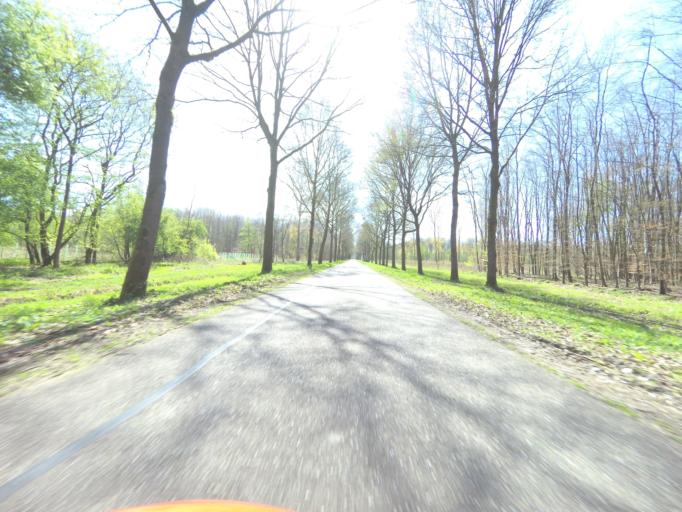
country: NL
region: Flevoland
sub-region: Gemeente Zeewolde
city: Zeewolde
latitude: 52.3101
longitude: 5.5067
